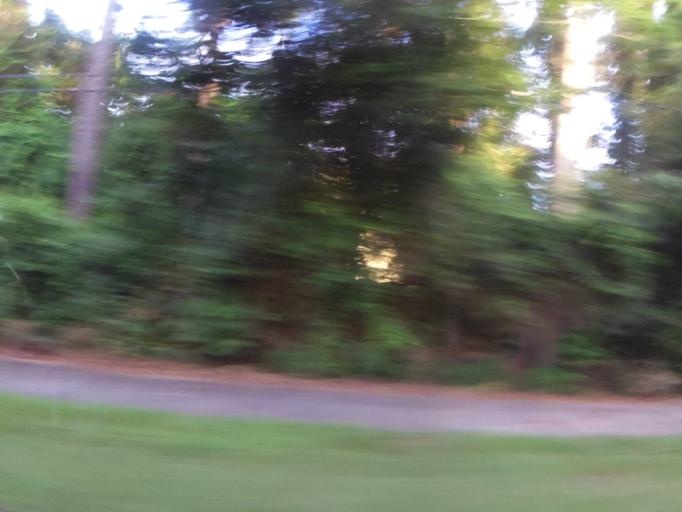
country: US
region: Florida
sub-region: Duval County
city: Atlantic Beach
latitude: 30.3768
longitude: -81.5029
